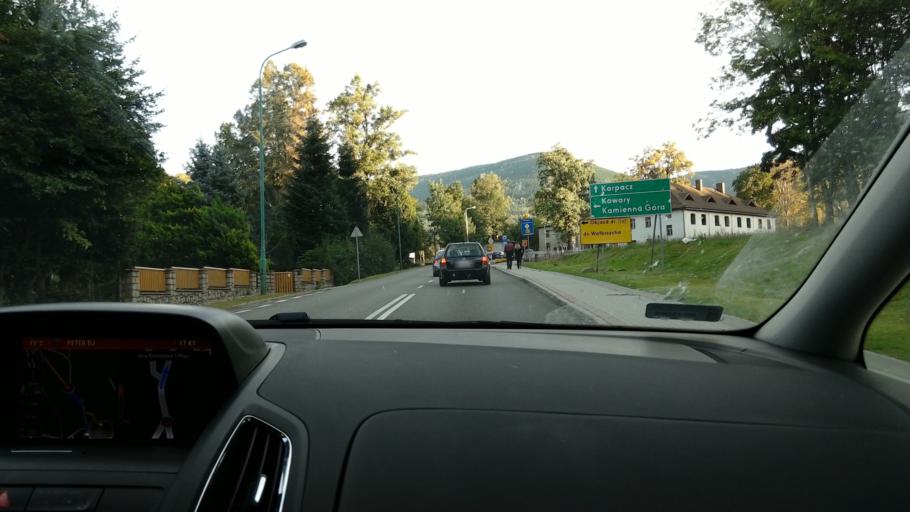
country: PL
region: Lower Silesian Voivodeship
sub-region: Powiat jeleniogorski
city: Karpacz
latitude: 50.7851
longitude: 15.7617
